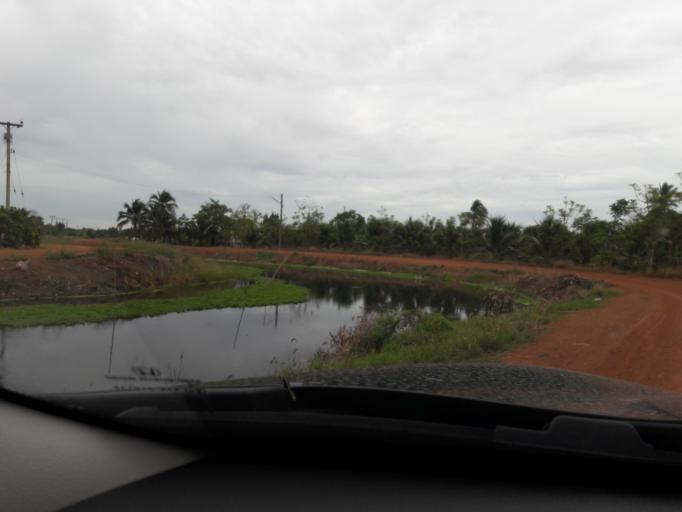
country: TH
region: Ratchaburi
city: Bang Phae
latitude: 13.6153
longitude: 99.9664
